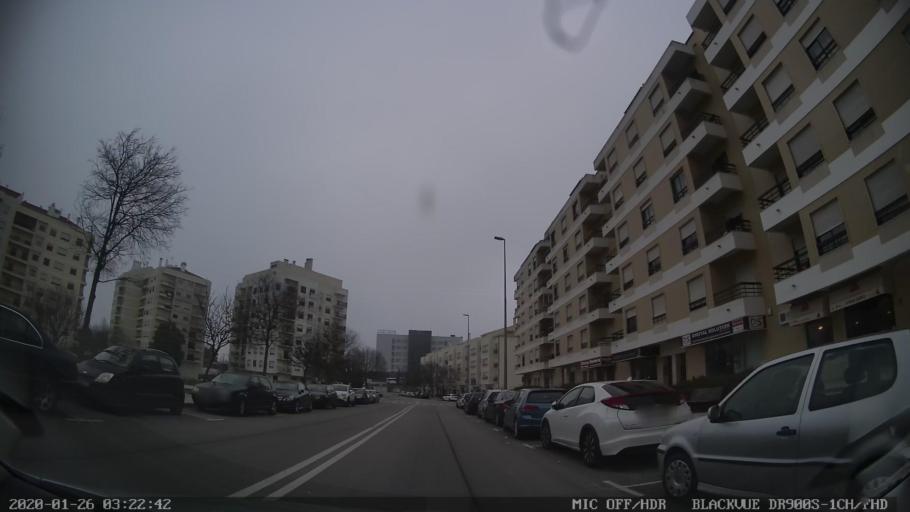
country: PT
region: Santarem
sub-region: Santarem
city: Santarem
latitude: 39.2247
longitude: -8.6909
